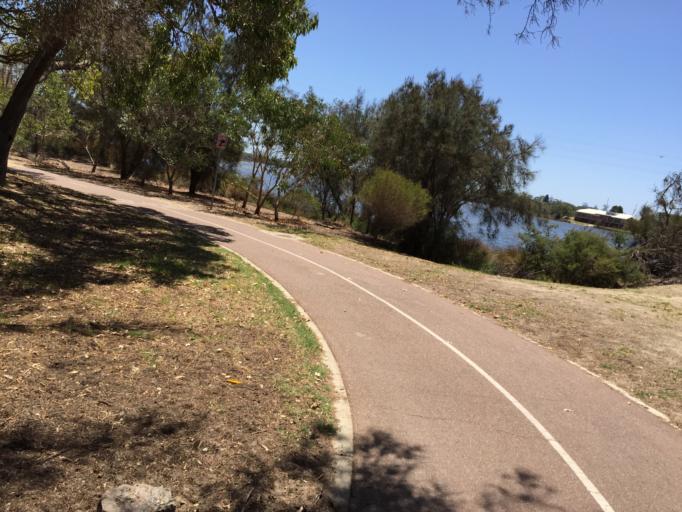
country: AU
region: Western Australia
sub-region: Canning
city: Wilson
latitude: -32.0240
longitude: 115.9007
